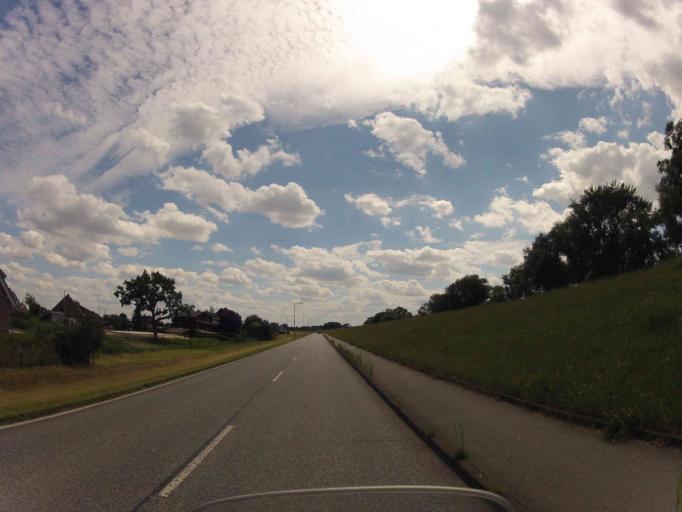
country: DE
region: Hamburg
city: Rothenburgsort
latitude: 53.4691
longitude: 10.0656
